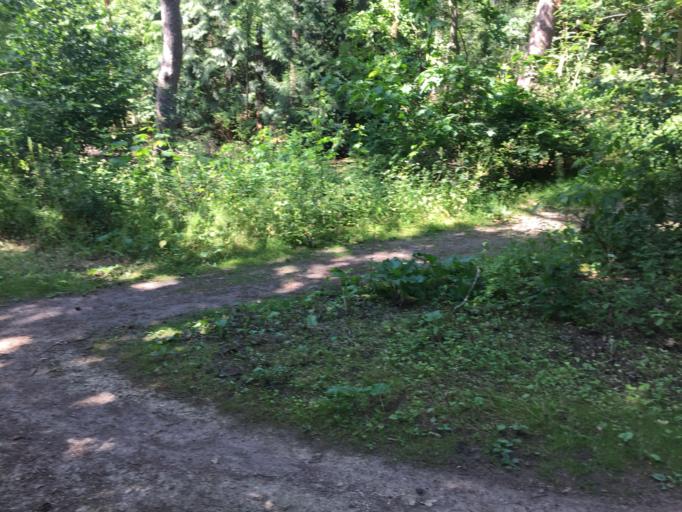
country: NL
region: Utrecht
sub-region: Gemeente Utrechtse Heuvelrug
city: Driebergen-Rijsenburg
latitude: 52.0856
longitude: 5.2686
